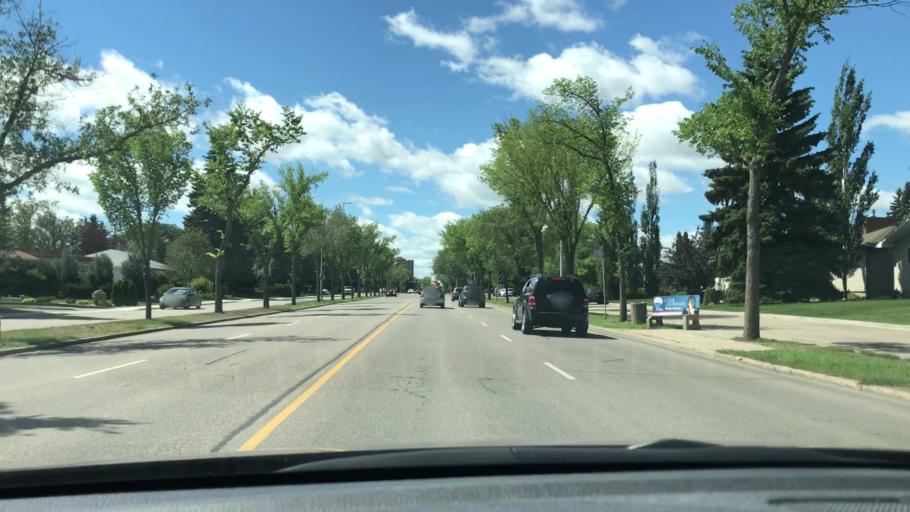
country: CA
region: Alberta
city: Edmonton
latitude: 53.5194
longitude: -113.5706
